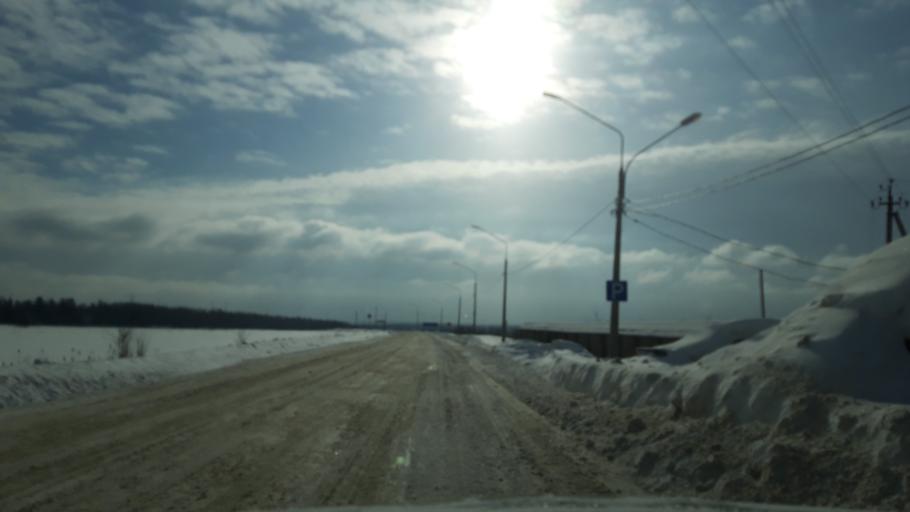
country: RU
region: Moskovskaya
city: Yermolino
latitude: 56.1377
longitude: 37.3783
